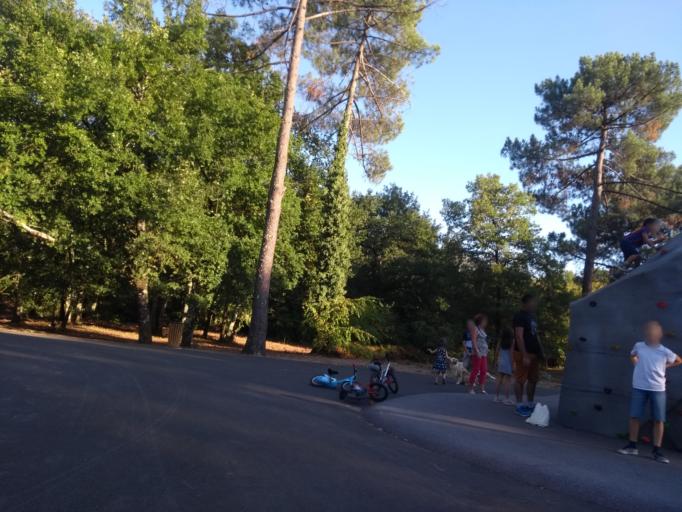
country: FR
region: Aquitaine
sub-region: Departement de la Gironde
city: Pessac
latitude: 44.8023
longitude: -0.6868
